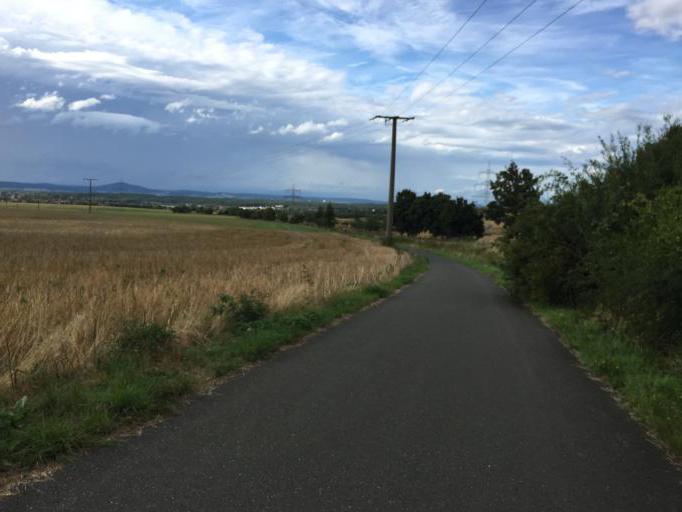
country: DE
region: Hesse
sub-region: Regierungsbezirk Giessen
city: Langgons
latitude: 50.5066
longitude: 8.6825
